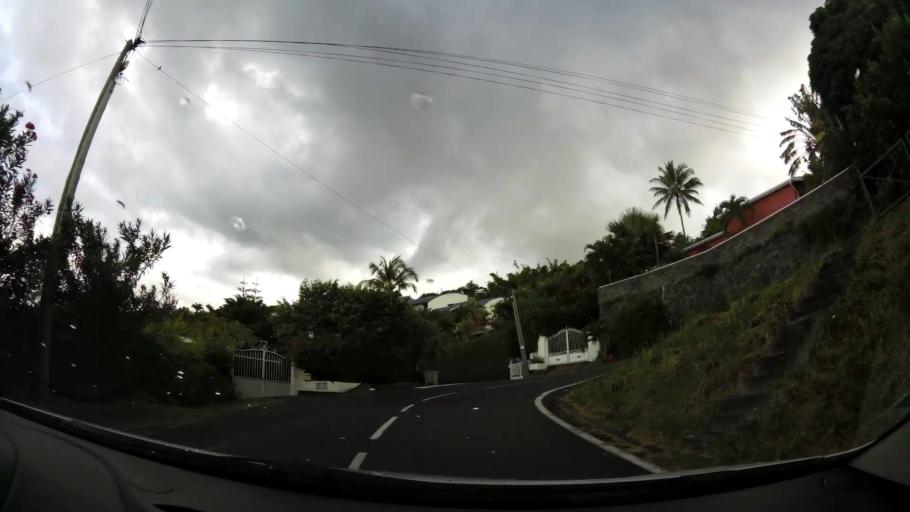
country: RE
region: Reunion
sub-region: Reunion
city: Saint-Denis
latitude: -20.9025
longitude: 55.4435
